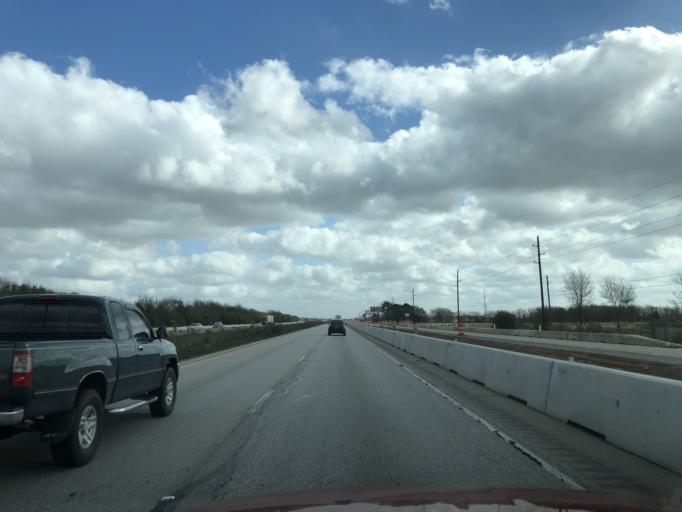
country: US
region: Texas
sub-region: Austin County
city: Sealy
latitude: 29.7754
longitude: -96.0945
